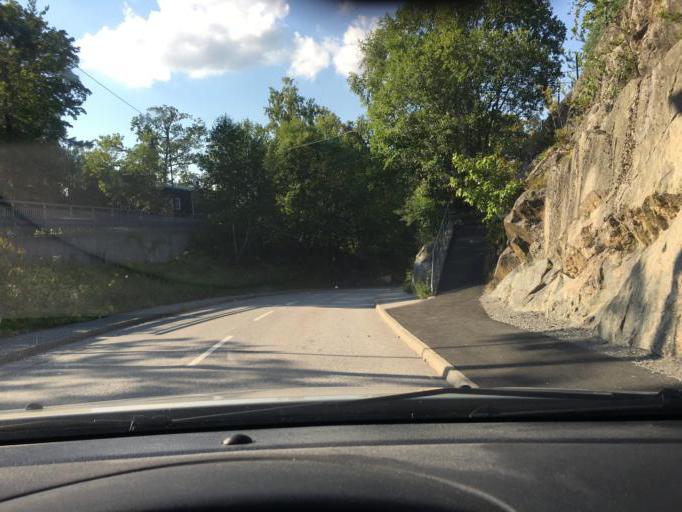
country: SE
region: Stockholm
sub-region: Lidingo
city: Brevik
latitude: 59.3191
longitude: 18.2293
